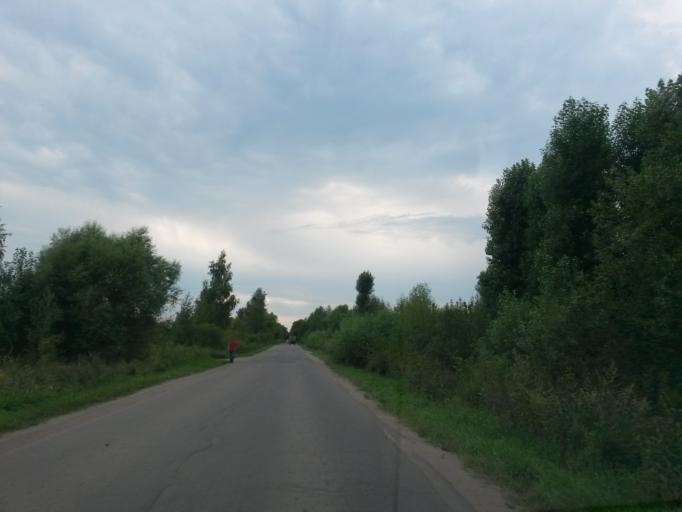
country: RU
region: Jaroslavl
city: Yaroslavl
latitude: 57.6073
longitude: 39.7880
